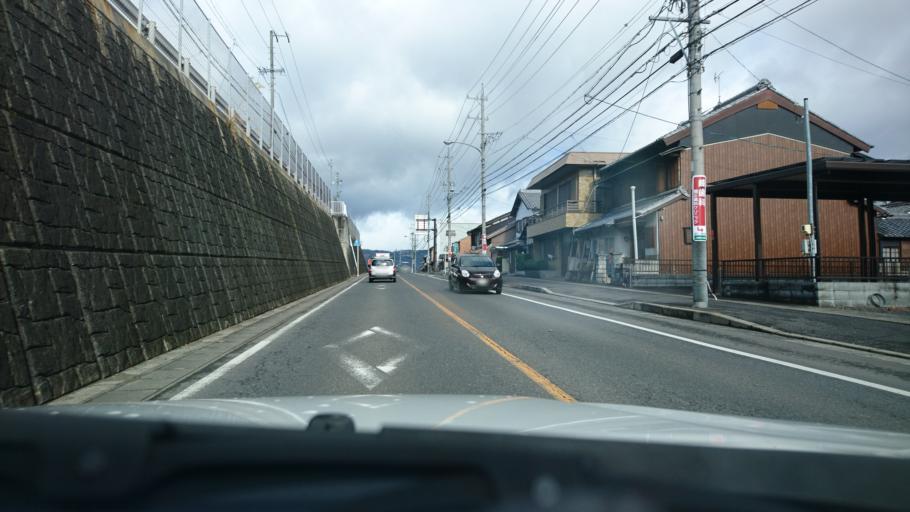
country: JP
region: Mie
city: Ueno-ebisumachi
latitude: 34.7683
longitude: 136.1233
